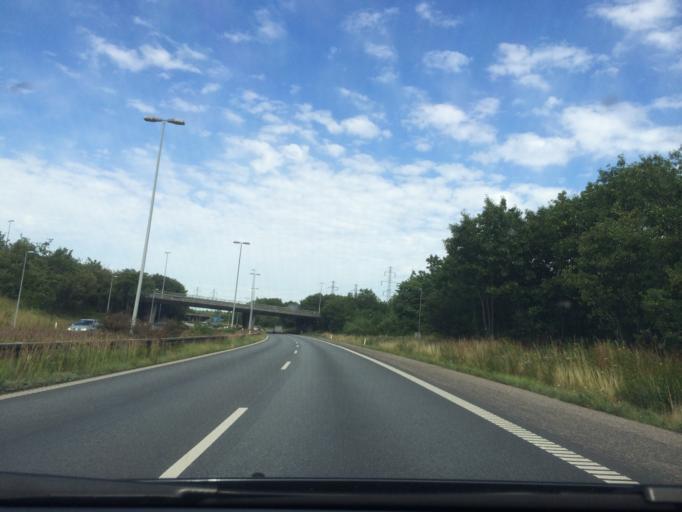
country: DK
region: Capital Region
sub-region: Brondby Kommune
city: Brondbyvester
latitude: 55.6293
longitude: 12.4327
